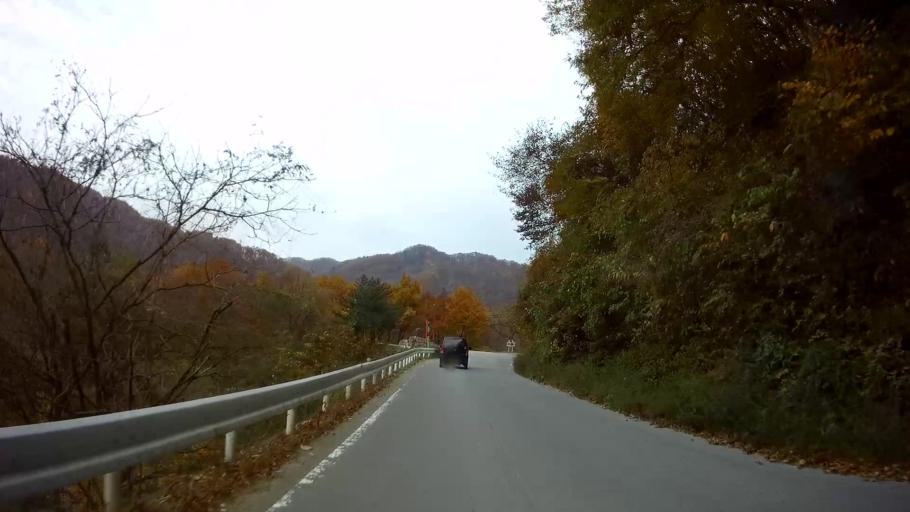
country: JP
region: Gunma
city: Nakanojomachi
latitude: 36.6292
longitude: 138.6501
